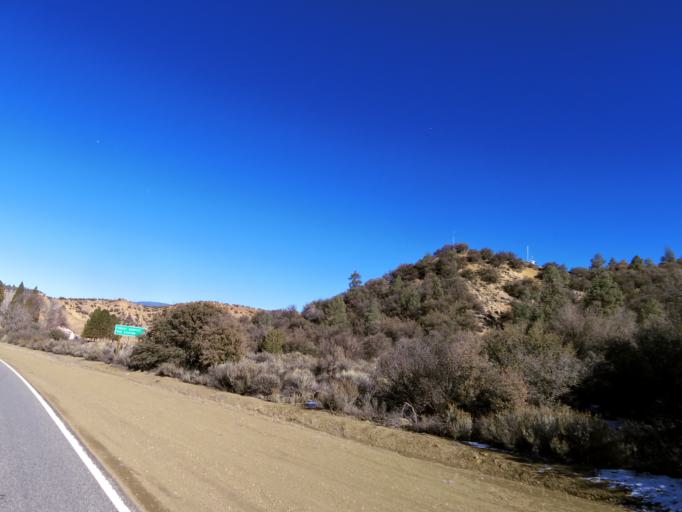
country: US
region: California
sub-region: Ventura County
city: Meiners Oaks
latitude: 34.6816
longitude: -119.3554
